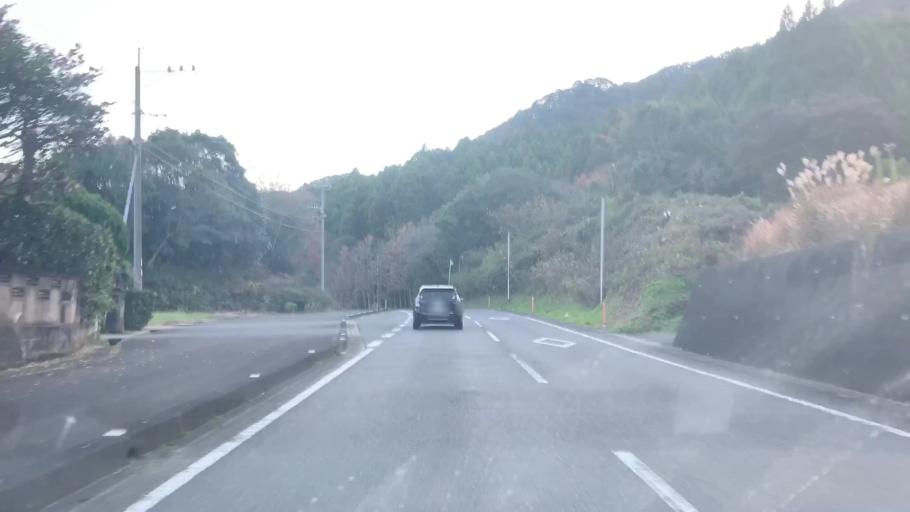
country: JP
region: Saga Prefecture
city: Imaricho-ko
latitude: 33.3212
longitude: 129.9693
